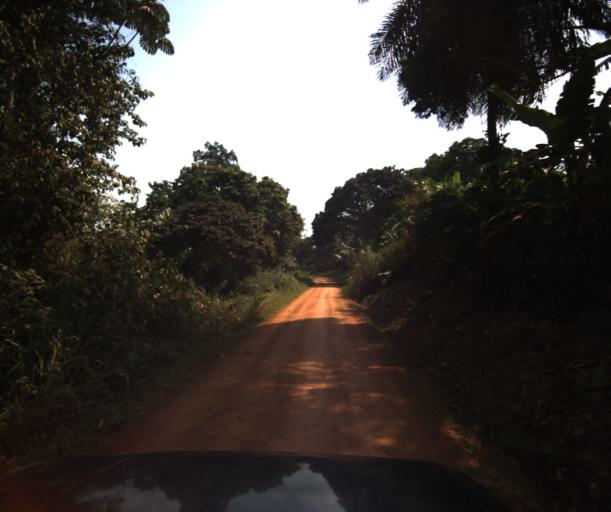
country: CM
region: Centre
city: Akono
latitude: 3.6000
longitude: 11.2380
